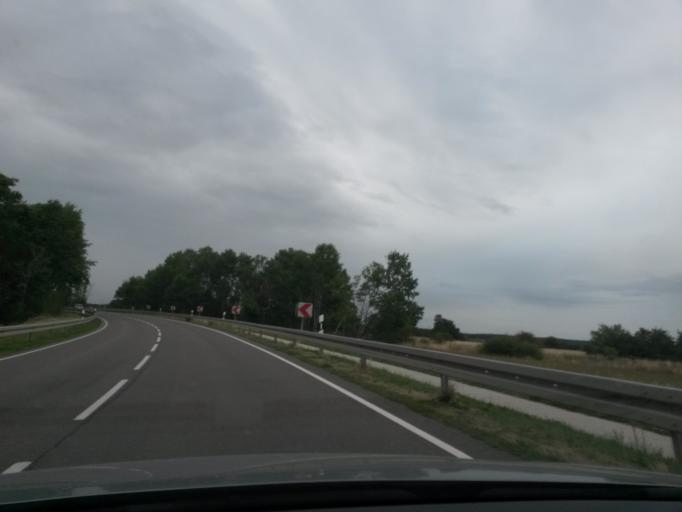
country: DE
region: Saxony-Anhalt
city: Klietz
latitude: 52.7002
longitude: 12.0729
